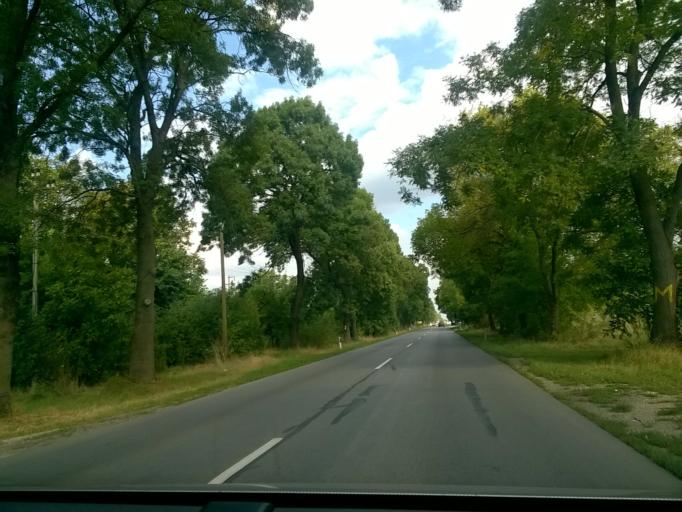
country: RS
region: Autonomna Pokrajina Vojvodina
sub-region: Juznobanatski Okrug
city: Pancevo
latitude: 44.9109
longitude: 20.6325
